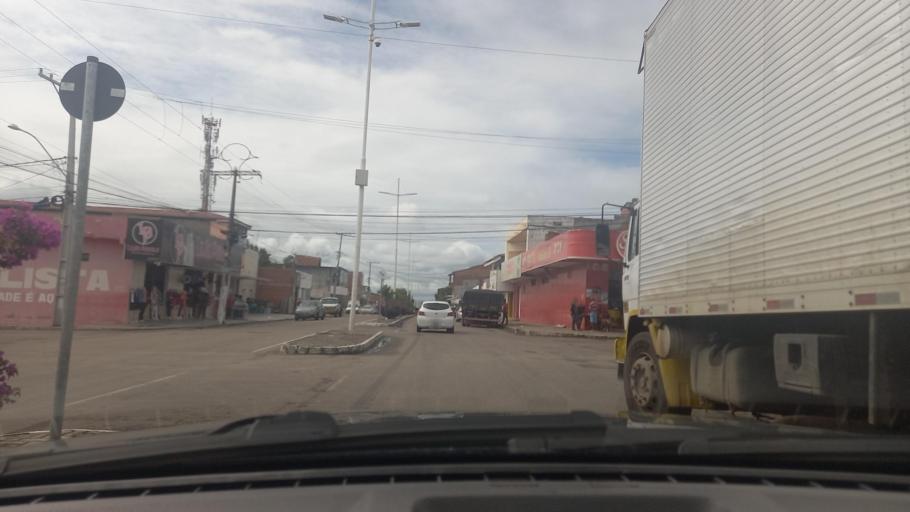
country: BR
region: Bahia
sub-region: Paulo Afonso
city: Paulo Afonso
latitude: -9.4410
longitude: -38.2140
